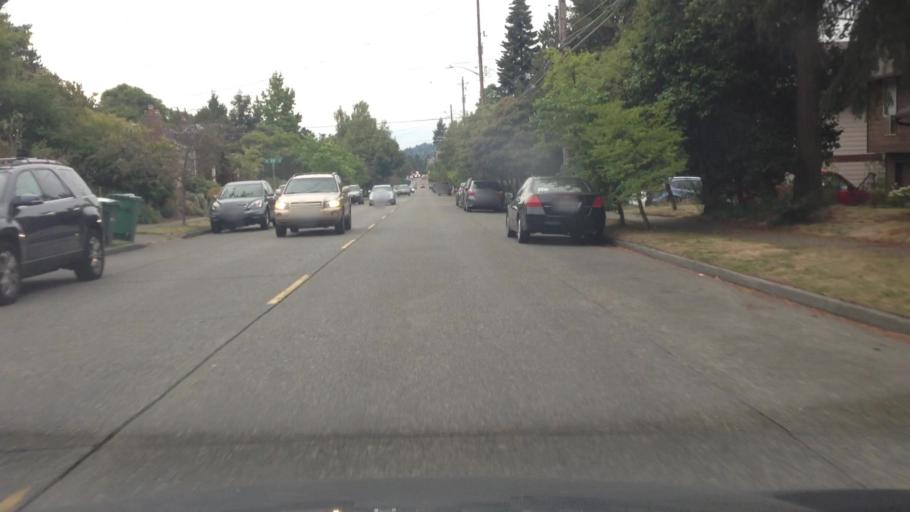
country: US
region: Washington
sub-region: King County
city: Inglewood-Finn Hill
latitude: 47.6717
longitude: -122.2849
